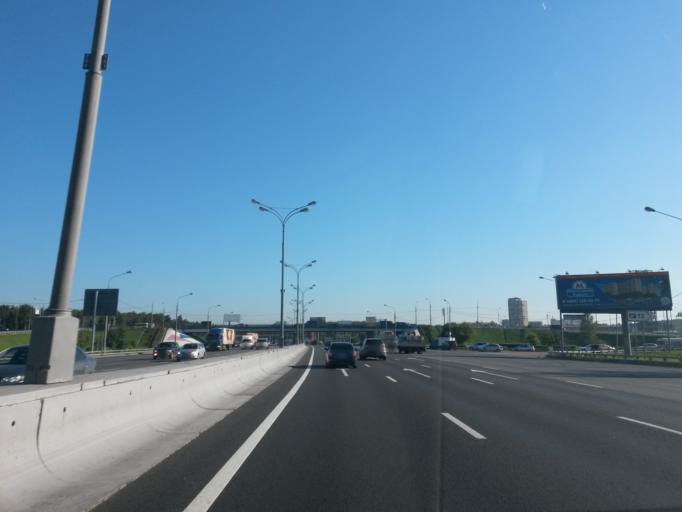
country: RU
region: Moskovskaya
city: Kotel'niki
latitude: 55.6550
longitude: 37.8383
